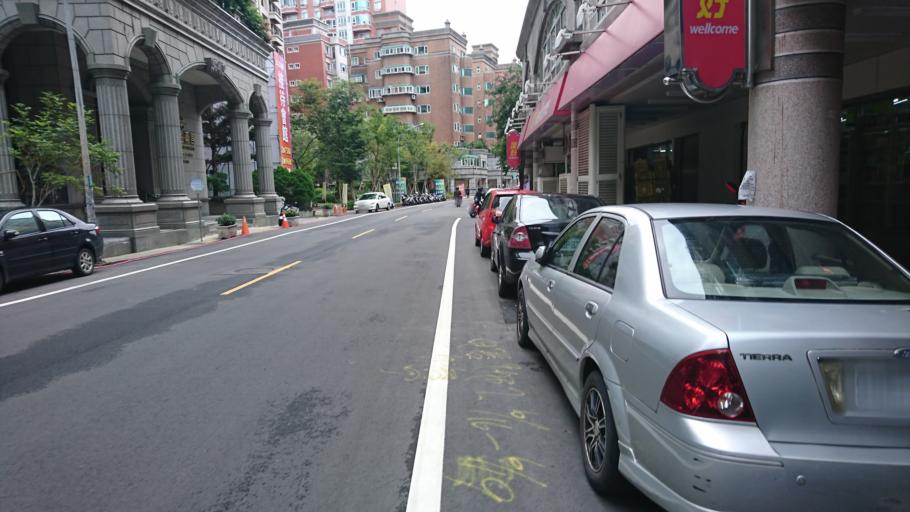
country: TW
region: Taiwan
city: Taoyuan City
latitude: 25.0573
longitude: 121.2964
